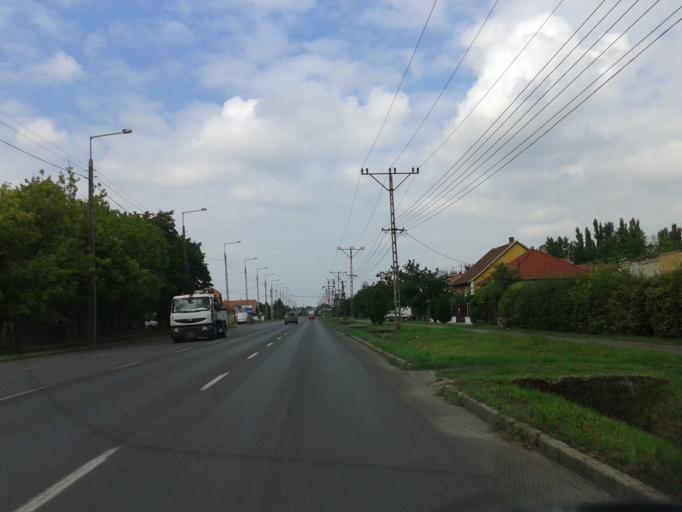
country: HU
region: Csongrad
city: Szeged
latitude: 46.2712
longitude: 20.0868
